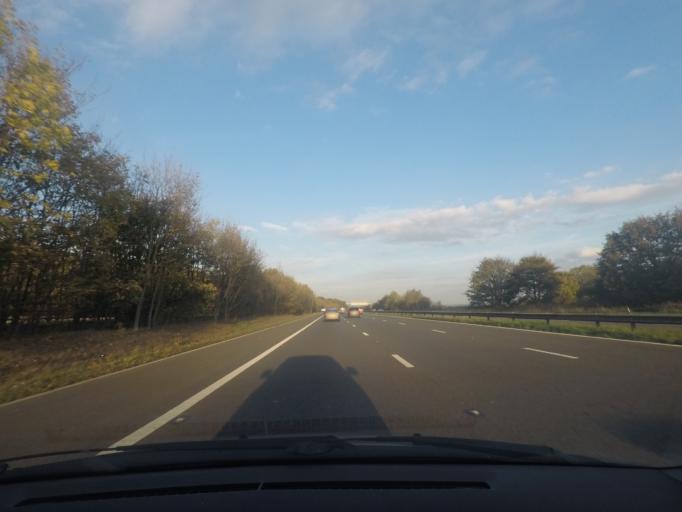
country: GB
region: England
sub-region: North Lincolnshire
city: Scawby
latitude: 53.5469
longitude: -0.5381
